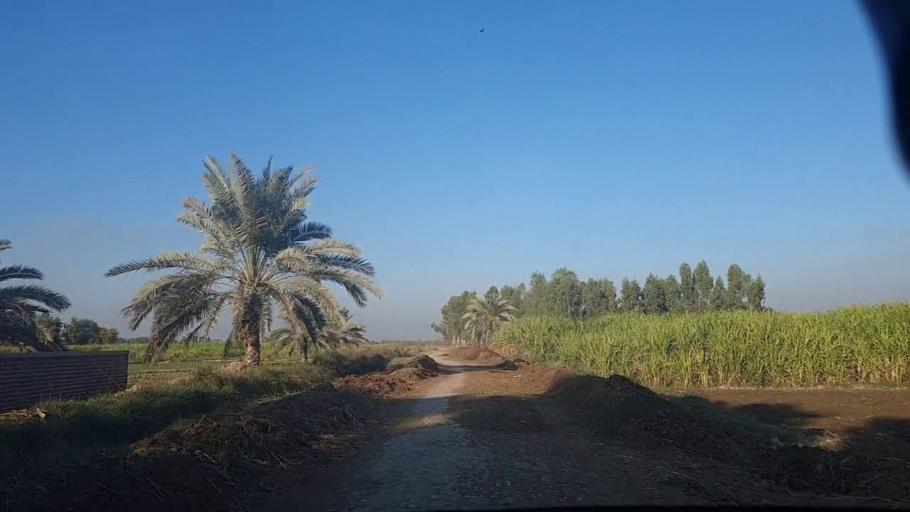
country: PK
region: Sindh
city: Sobhadero
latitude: 27.4013
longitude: 68.4210
